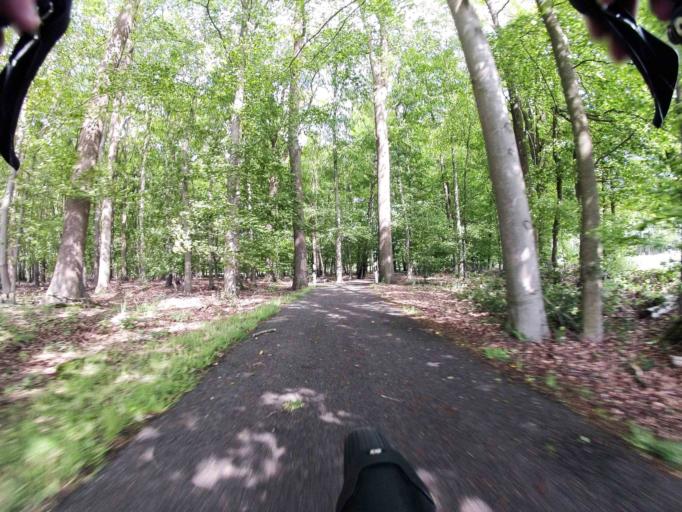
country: DE
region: North Rhine-Westphalia
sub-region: Regierungsbezirk Munster
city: Westerkappeln
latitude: 52.2815
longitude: 7.8636
